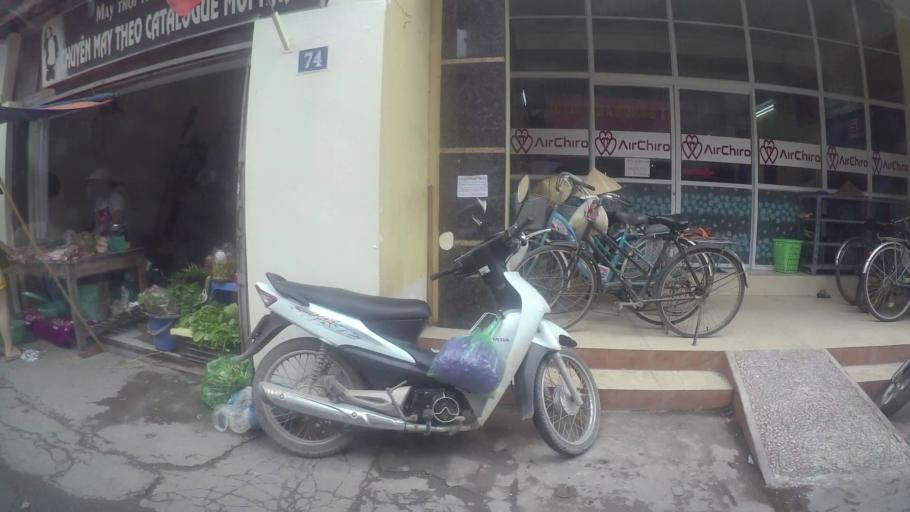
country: VN
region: Ha Noi
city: Tay Ho
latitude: 21.0708
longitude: 105.8009
